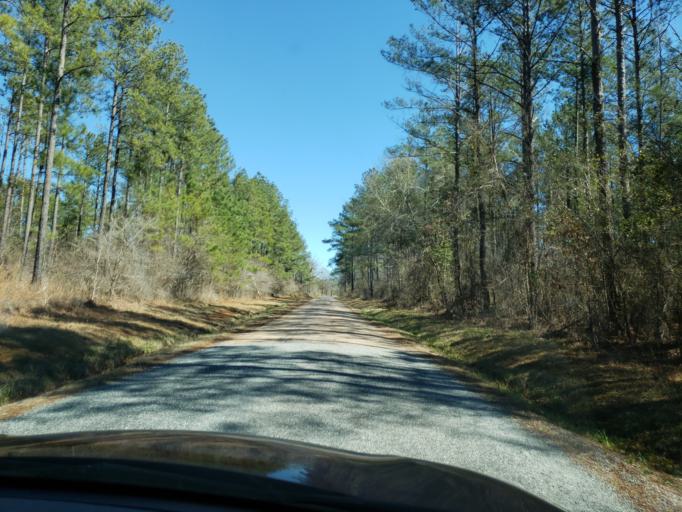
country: US
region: Alabama
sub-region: Elmore County
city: Tallassee
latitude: 32.6700
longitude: -85.8832
